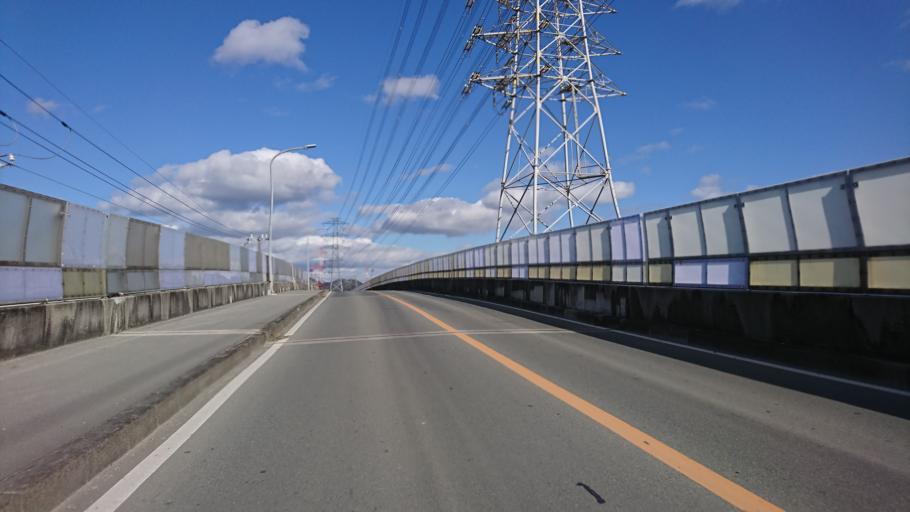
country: JP
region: Hyogo
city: Kakogawacho-honmachi
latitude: 34.7730
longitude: 134.7771
